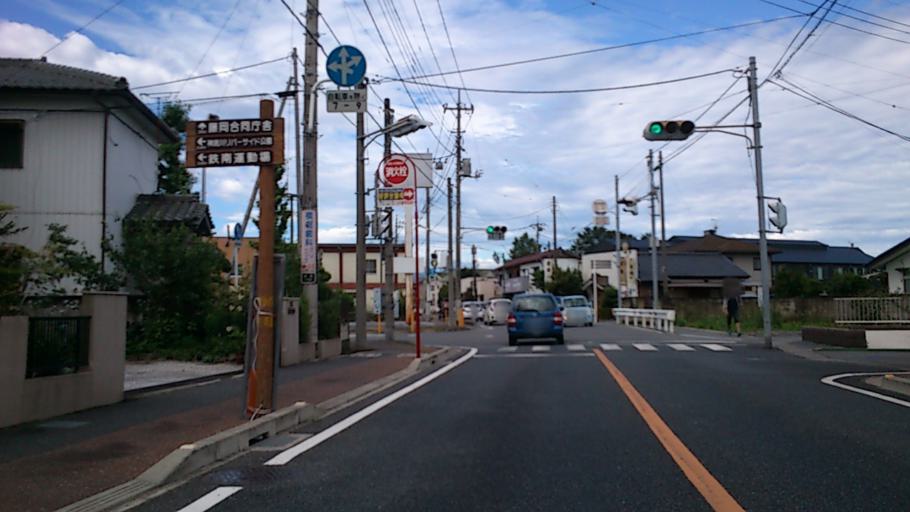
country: JP
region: Gunma
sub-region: Sawa-gun
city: Tamamura
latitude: 36.2704
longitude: 139.1058
